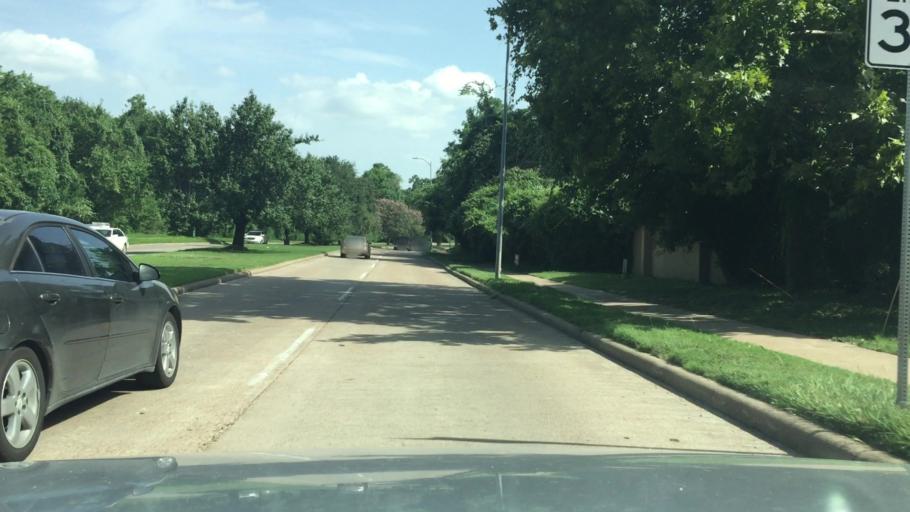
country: US
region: Texas
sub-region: Harris County
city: Bunker Hill Village
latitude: 29.7648
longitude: -95.5760
